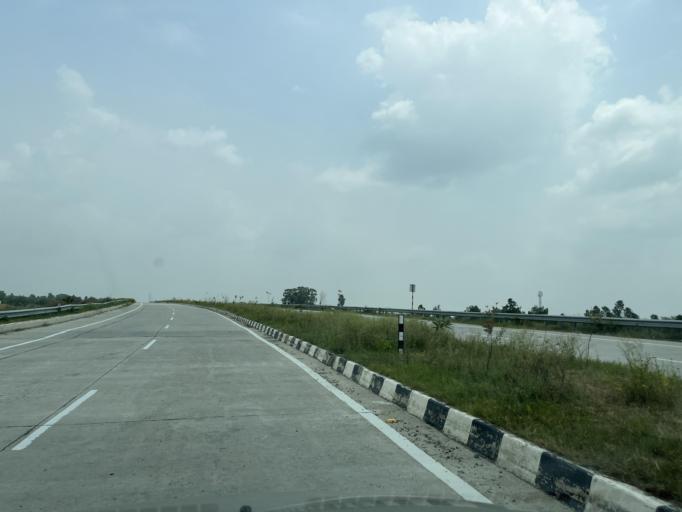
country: IN
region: Uttar Pradesh
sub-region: Bijnor
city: Nagina
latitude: 29.4248
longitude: 78.4259
